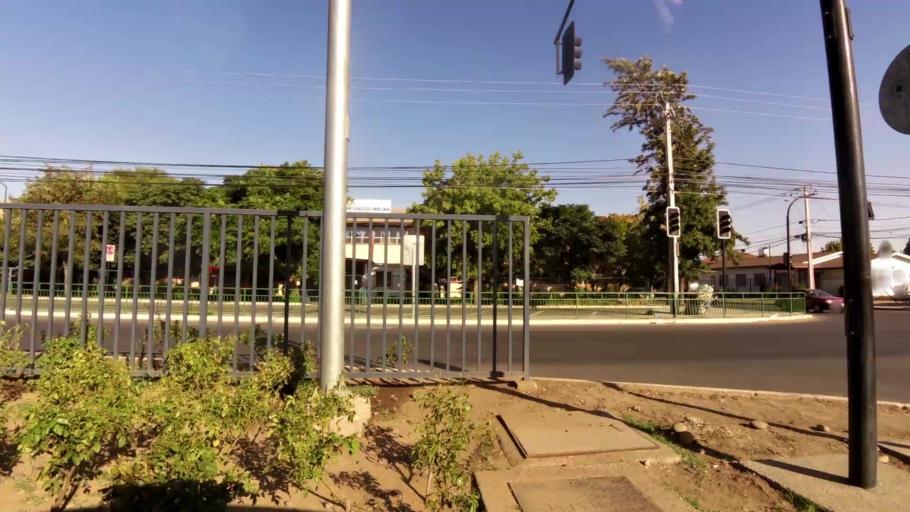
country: CL
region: Maule
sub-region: Provincia de Talca
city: Talca
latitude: -35.4423
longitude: -71.6852
